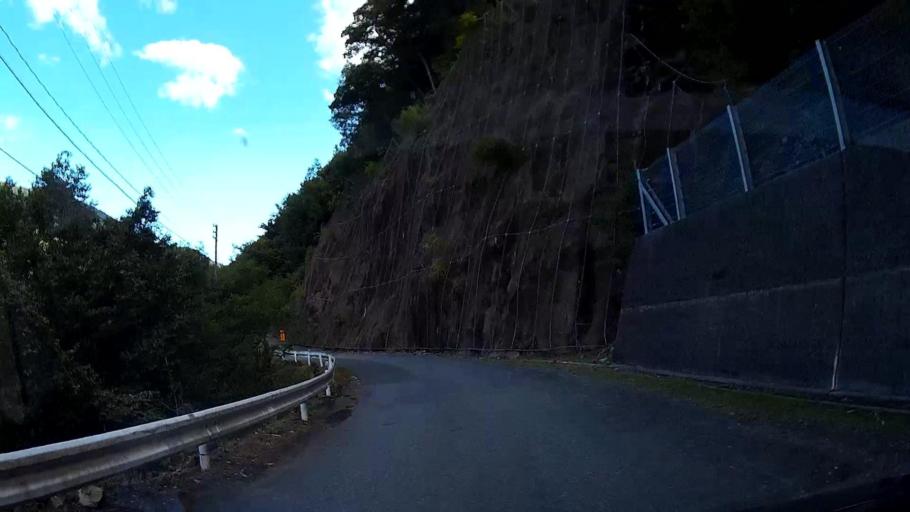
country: JP
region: Shizuoka
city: Shizuoka-shi
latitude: 35.3038
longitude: 138.2148
